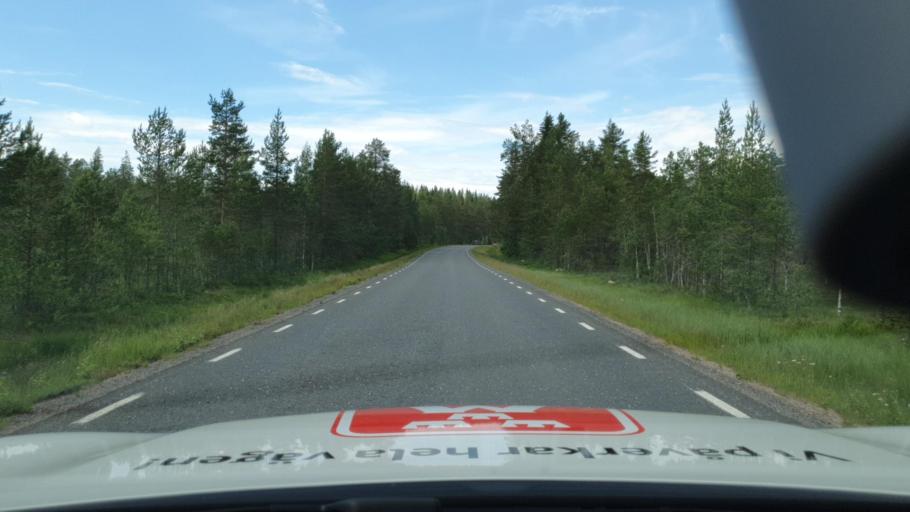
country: SE
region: Vaermland
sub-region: Torsby Kommun
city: Torsby
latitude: 60.5309
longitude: 12.8219
